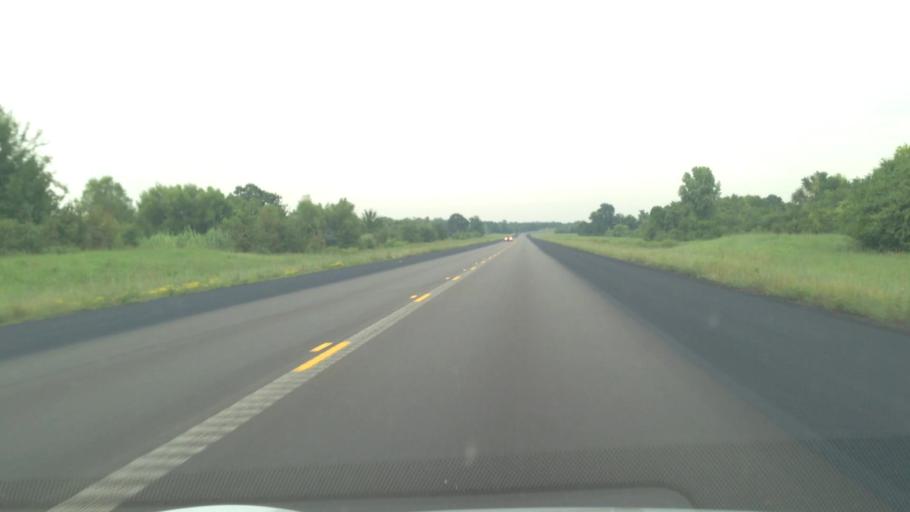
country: US
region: Kansas
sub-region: Cherokee County
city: Baxter Springs
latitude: 37.0363
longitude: -94.7074
